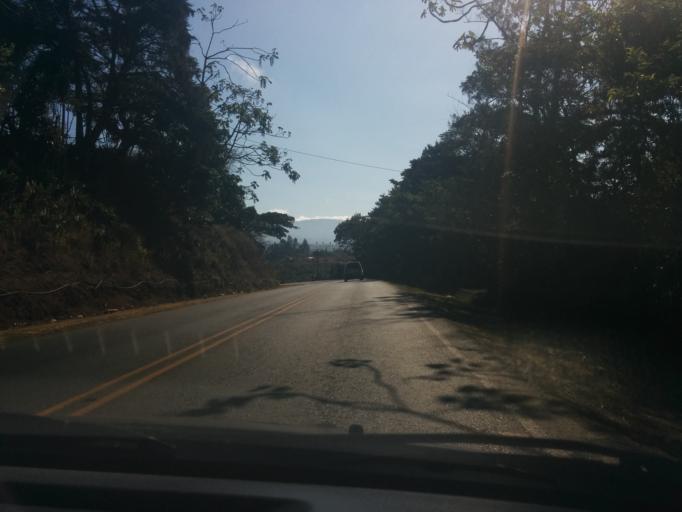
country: CR
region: Alajuela
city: San Rafael
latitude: 10.0725
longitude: -84.4841
